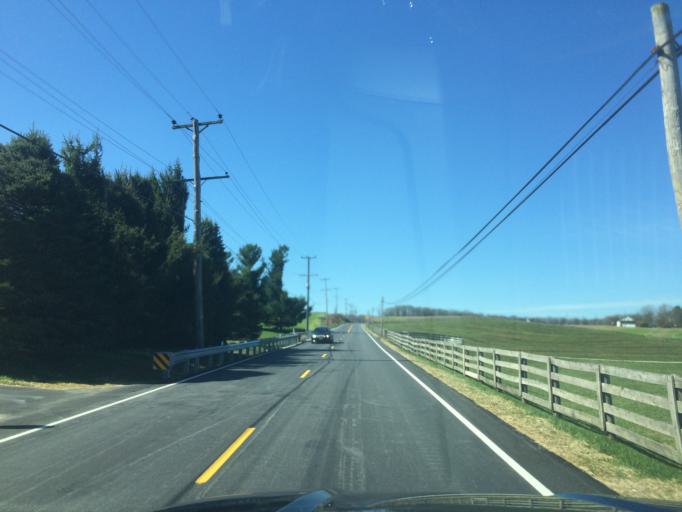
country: US
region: Maryland
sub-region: Carroll County
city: Westminster
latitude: 39.6289
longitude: -76.9943
